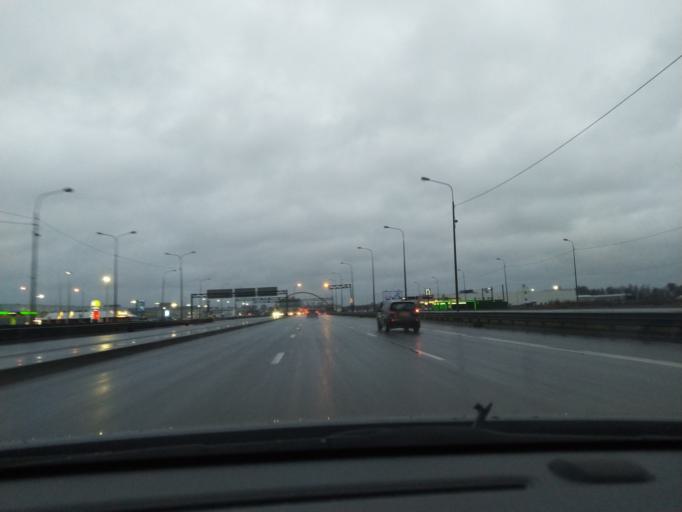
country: RU
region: St.-Petersburg
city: Sosnovaya Polyana
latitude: 59.8041
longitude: 30.1618
